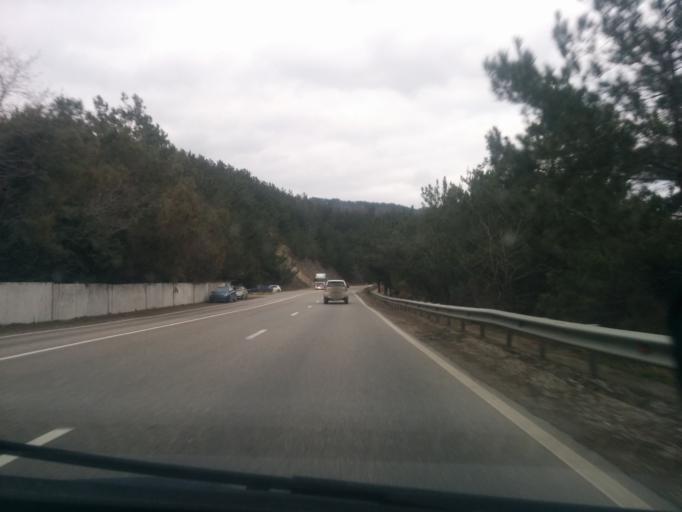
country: RU
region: Krasnodarskiy
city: Ol'ginka
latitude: 44.1869
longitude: 38.9052
